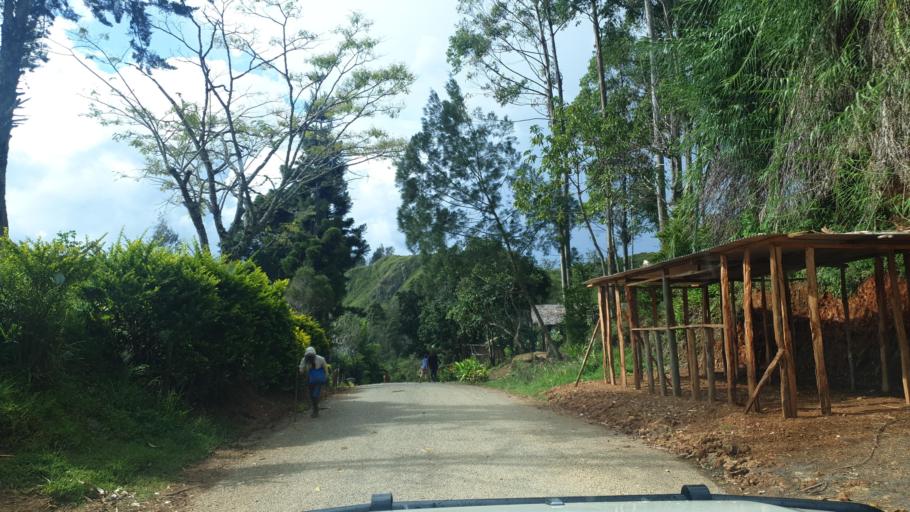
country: PG
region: Chimbu
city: Kundiawa
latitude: -6.1594
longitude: 145.1341
